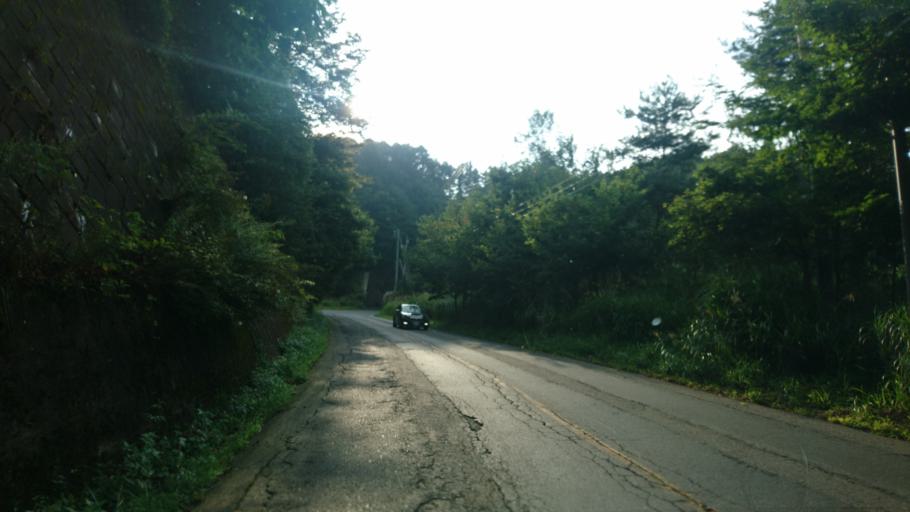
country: JP
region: Gunma
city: Omamacho-omama
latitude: 36.6096
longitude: 139.2329
